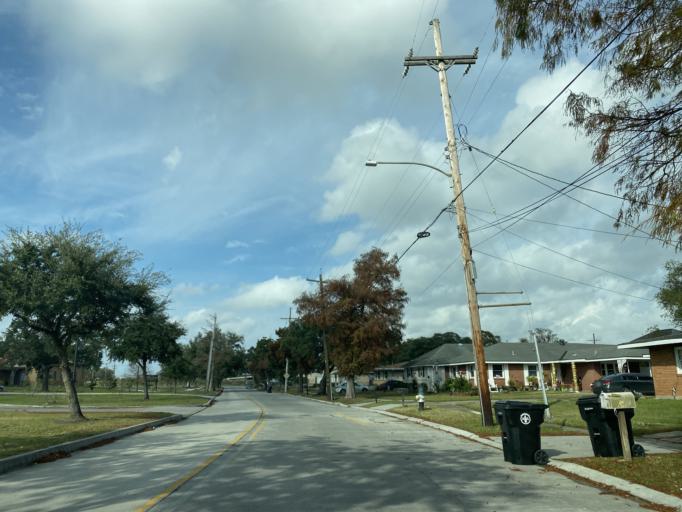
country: US
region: Louisiana
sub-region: Saint Bernard Parish
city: Arabi
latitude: 30.0275
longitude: -90.0382
